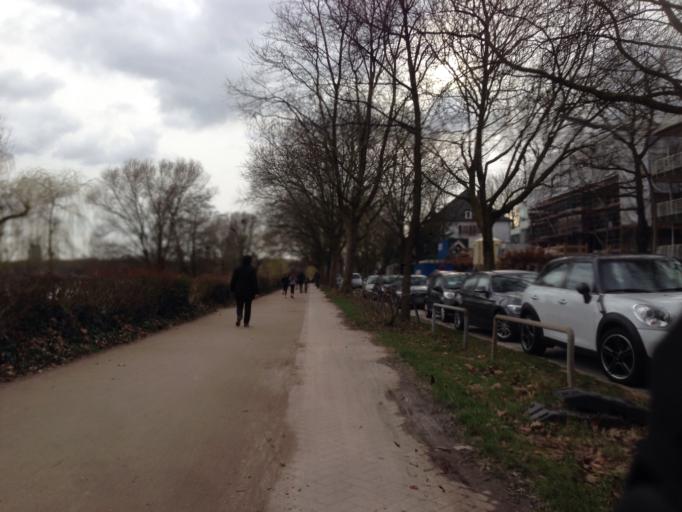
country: DE
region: Hamburg
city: Hamburg
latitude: 53.5777
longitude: 10.0081
